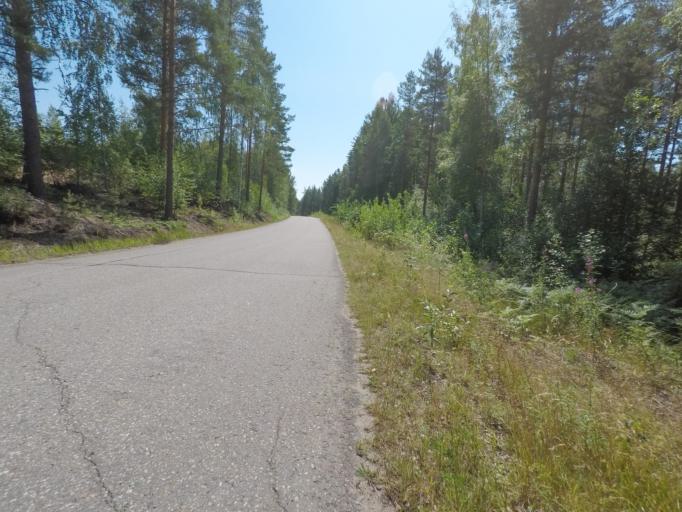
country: FI
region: Southern Savonia
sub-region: Mikkeli
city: Puumala
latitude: 61.4384
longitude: 28.1667
